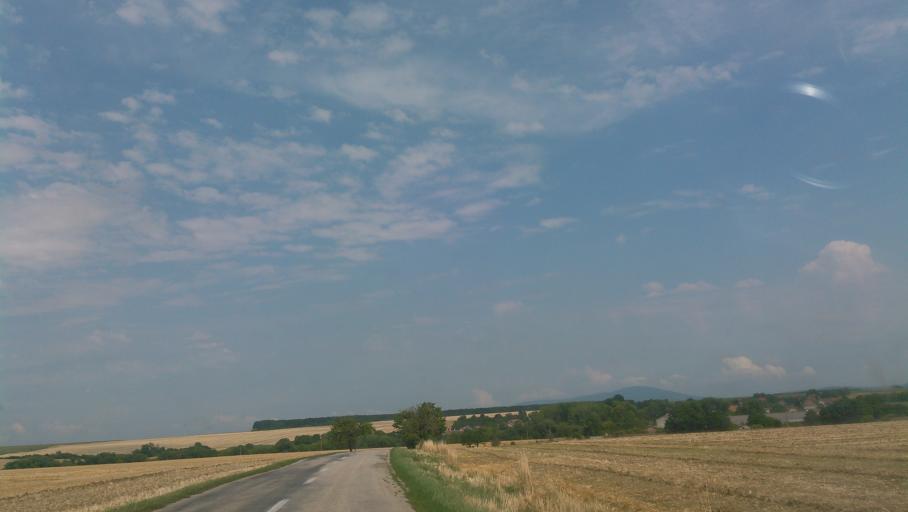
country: SK
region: Trnavsky
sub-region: Okres Trnava
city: Piestany
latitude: 48.5035
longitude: 18.0010
